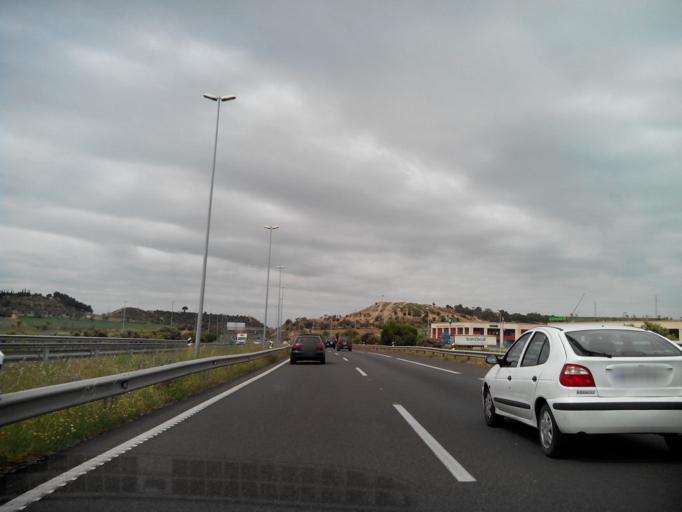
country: ES
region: Catalonia
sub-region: Provincia de Lleida
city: Tarrega
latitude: 41.6610
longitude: 1.1349
